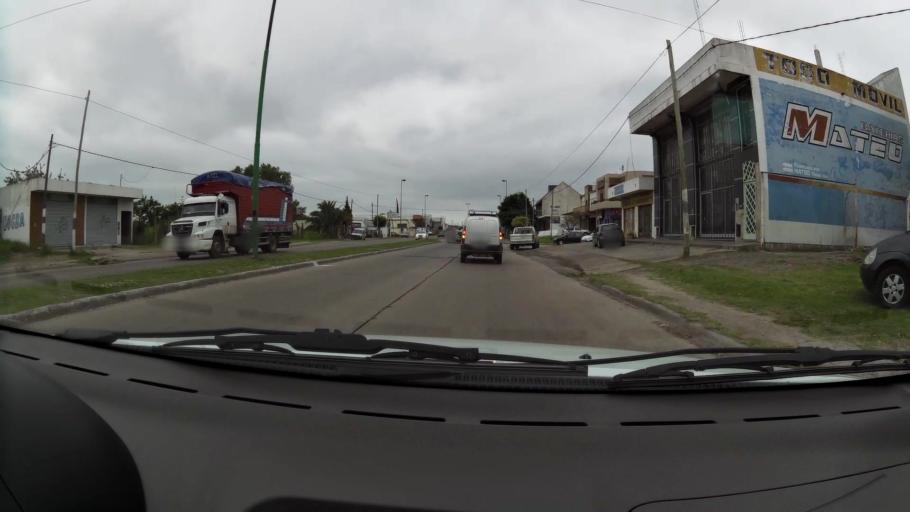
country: AR
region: Buenos Aires
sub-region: Partido de La Plata
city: La Plata
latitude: -34.9868
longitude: -58.0387
